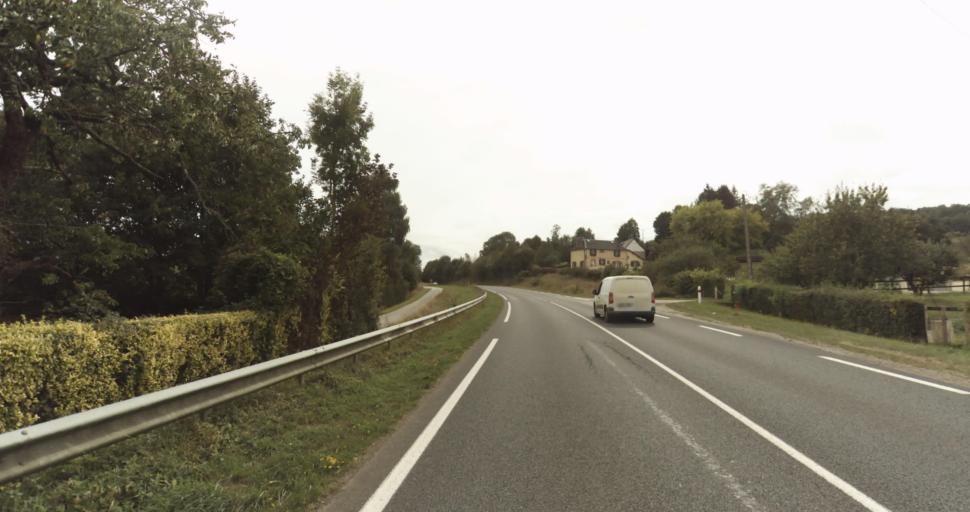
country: FR
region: Lower Normandy
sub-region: Departement de l'Orne
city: Gace
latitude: 48.8171
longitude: 0.2805
